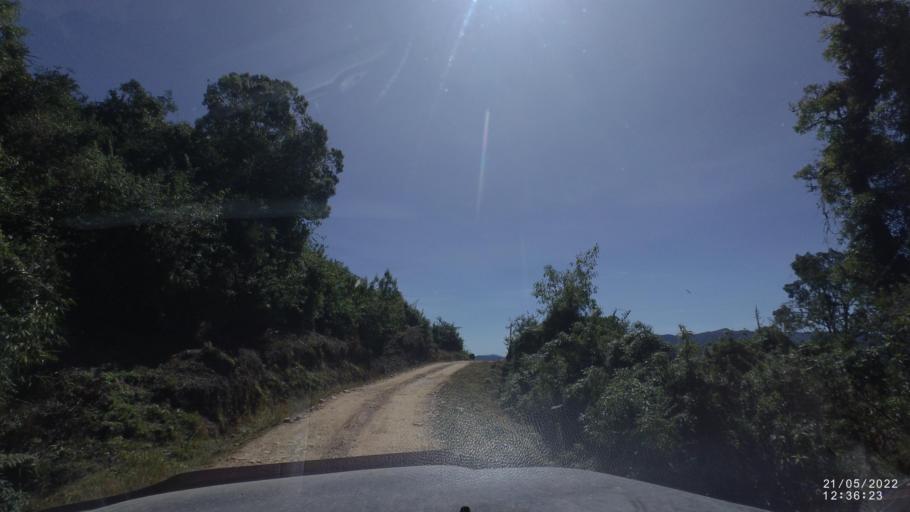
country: BO
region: Cochabamba
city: Colomi
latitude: -17.2040
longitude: -65.9177
